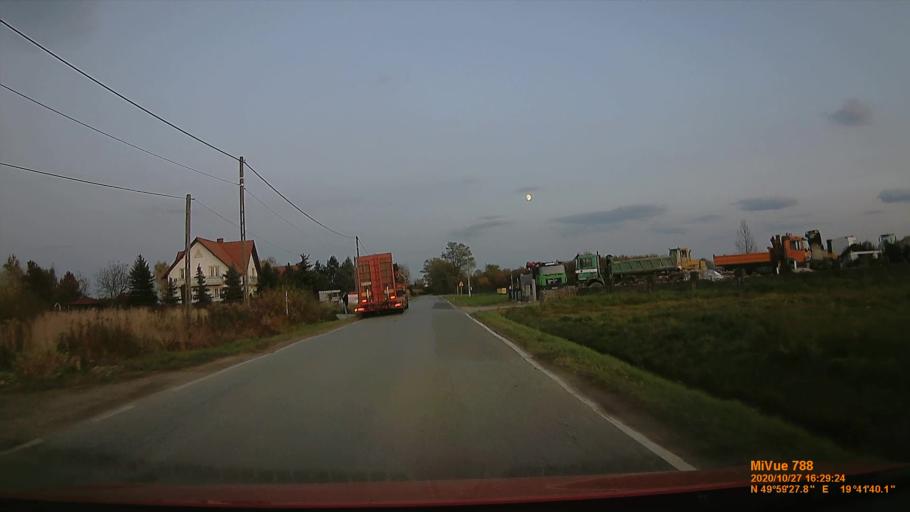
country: PL
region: Lesser Poland Voivodeship
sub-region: Powiat krakowski
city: Czernichow
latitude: 49.9910
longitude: 19.6946
